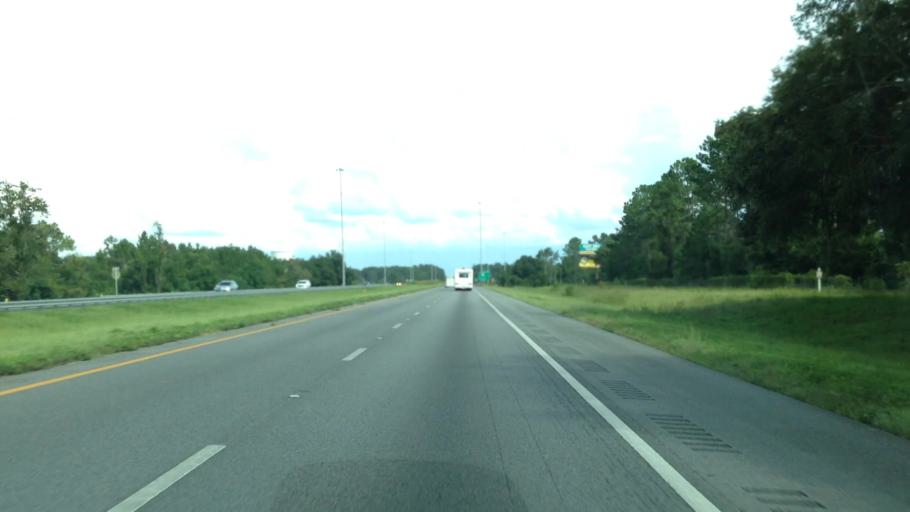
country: US
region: Florida
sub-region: Suwannee County
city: Live Oak
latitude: 30.3362
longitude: -82.9704
